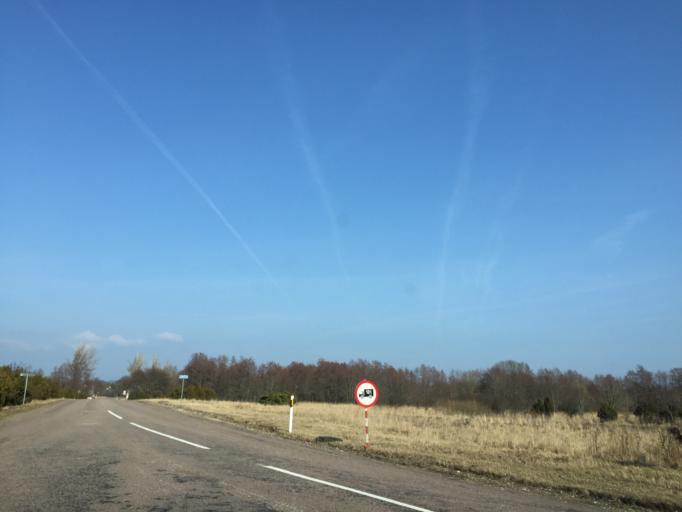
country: EE
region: Saare
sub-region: Kuressaare linn
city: Kuressaare
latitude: 58.0026
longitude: 22.0387
